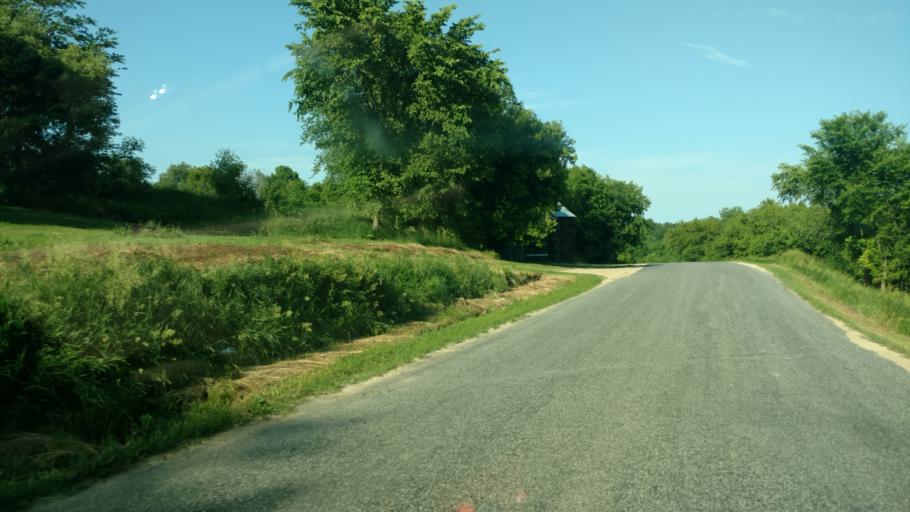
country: US
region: Wisconsin
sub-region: Vernon County
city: Hillsboro
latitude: 43.6822
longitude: -90.3565
